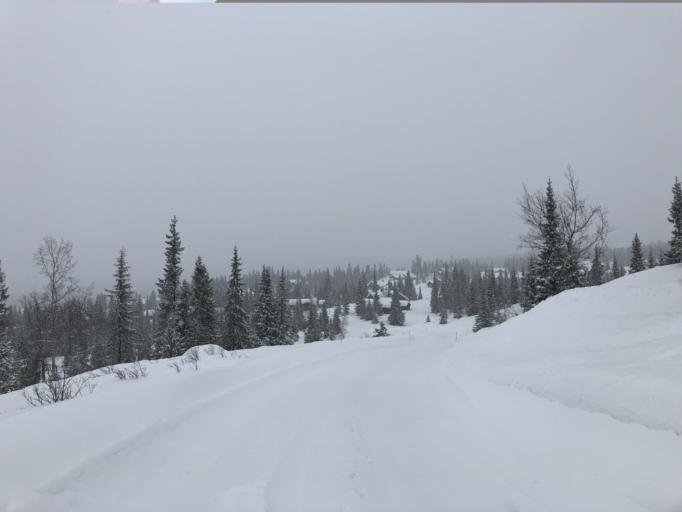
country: NO
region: Oppland
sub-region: Gausdal
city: Segalstad bru
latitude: 61.3282
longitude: 10.0551
